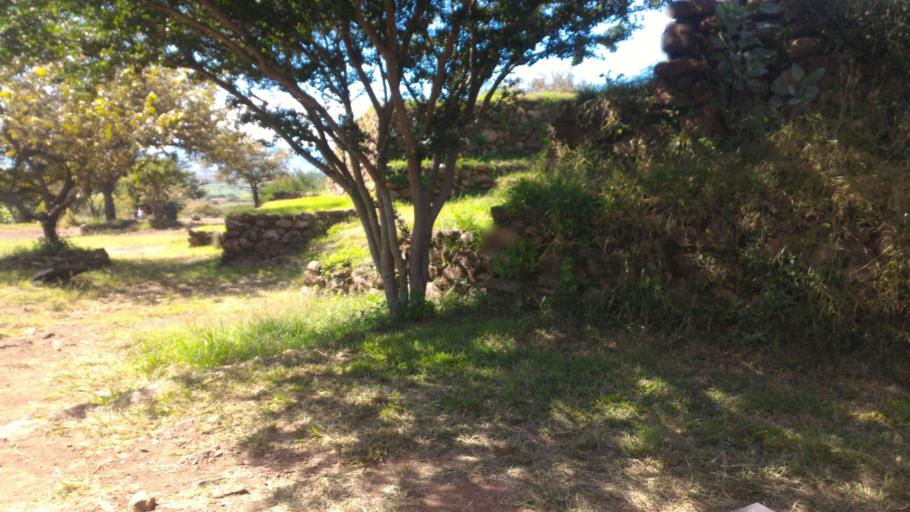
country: MX
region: Jalisco
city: Teuchitlan
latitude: 20.6954
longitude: -103.8360
